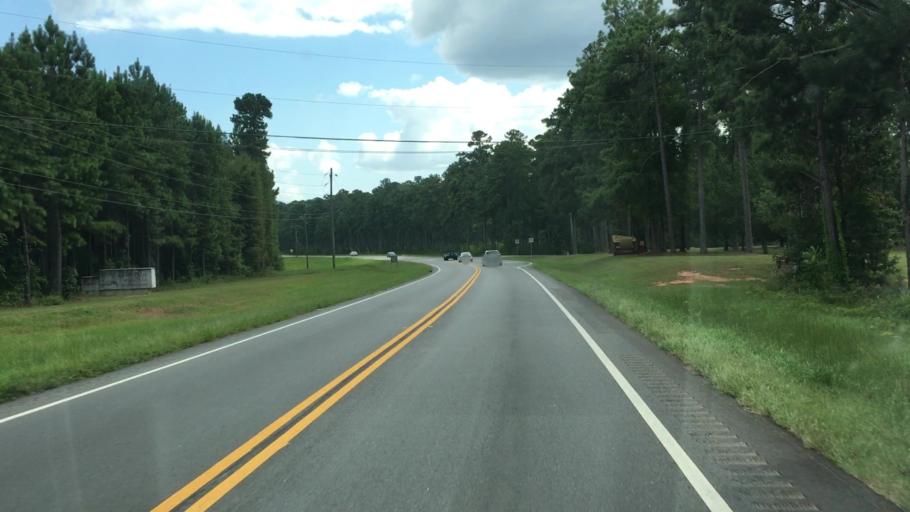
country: US
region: Georgia
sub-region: Putnam County
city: Jefferson
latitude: 33.4144
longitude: -83.3722
